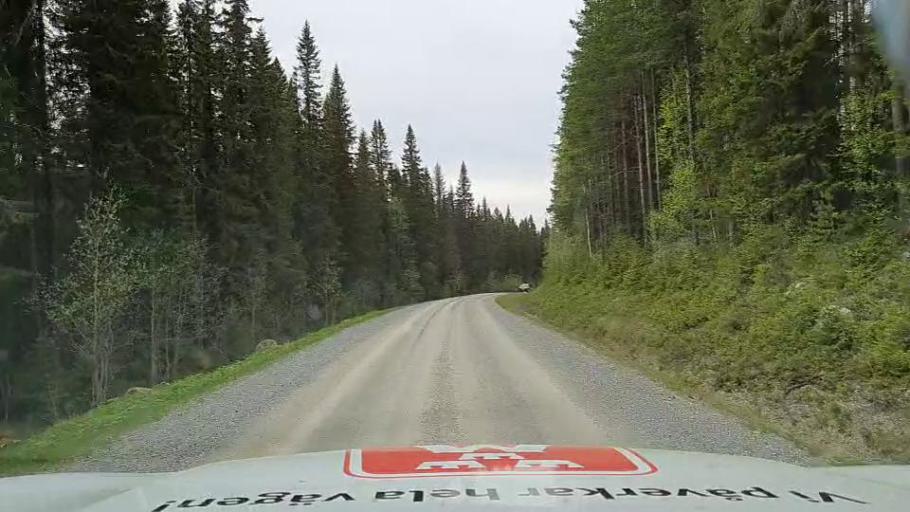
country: SE
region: Jaemtland
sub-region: OEstersunds Kommun
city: Brunflo
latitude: 62.6358
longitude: 14.9362
